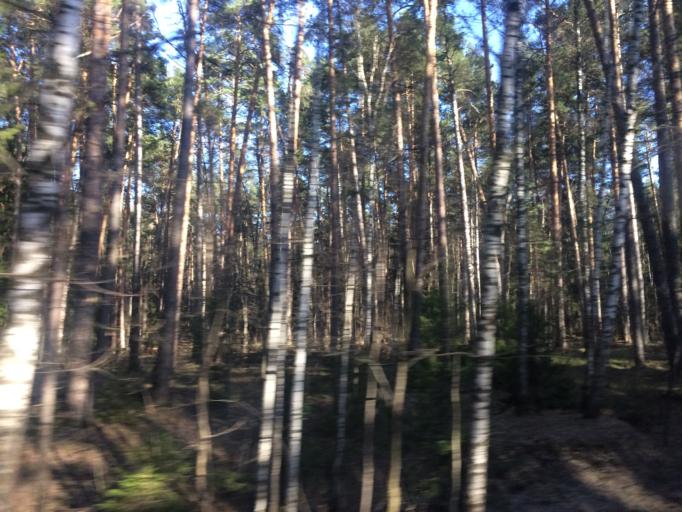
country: RU
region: Tatarstan
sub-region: Zelenodol'skiy Rayon
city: Vasil'yevo
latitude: 55.8907
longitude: 48.7259
